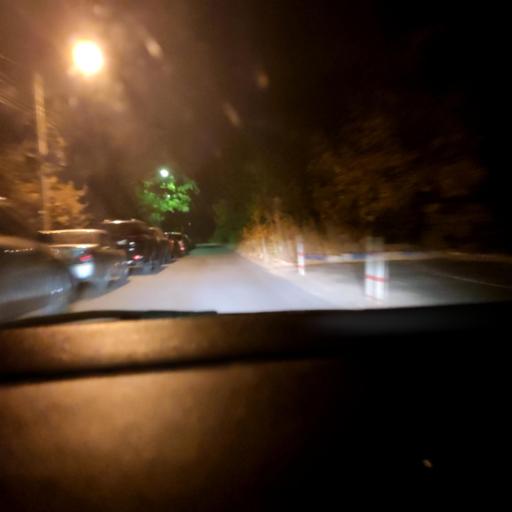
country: RU
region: Voronezj
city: Voronezh
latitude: 51.7030
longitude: 39.2232
